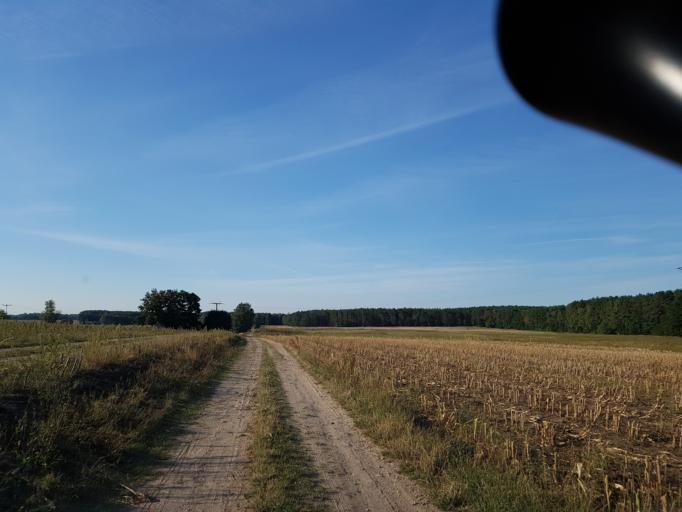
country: DE
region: Brandenburg
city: Hohenleipisch
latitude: 51.4890
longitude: 13.5265
